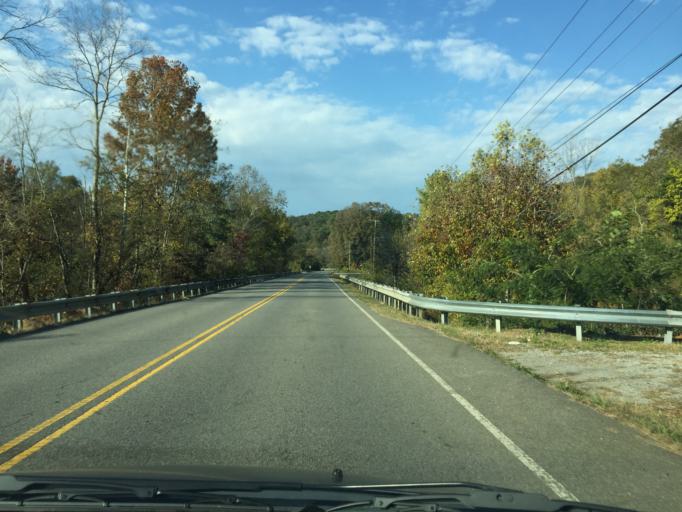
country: US
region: Tennessee
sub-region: Loudon County
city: Loudon
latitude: 35.7028
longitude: -84.3432
